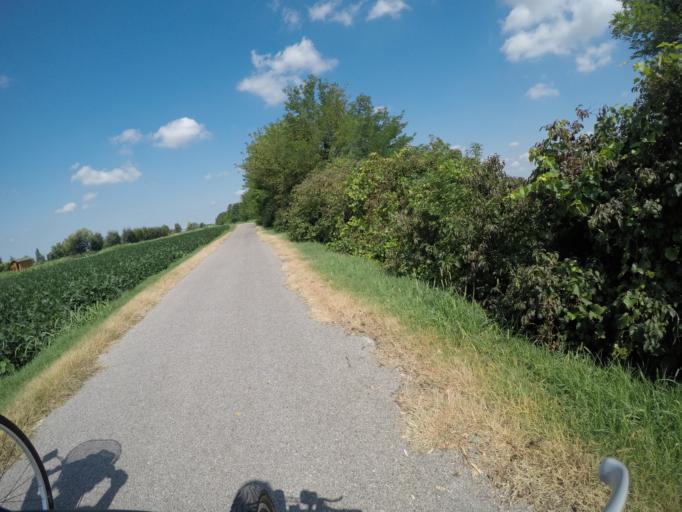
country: IT
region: Veneto
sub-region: Provincia di Rovigo
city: Villanova del Ghebbo Canton
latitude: 45.0631
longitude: 11.6251
